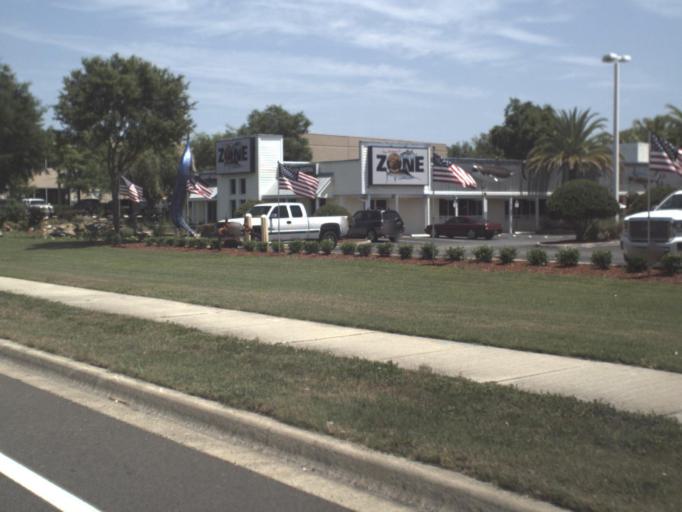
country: US
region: Florida
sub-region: Duval County
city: Neptune Beach
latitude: 30.2869
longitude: -81.5158
